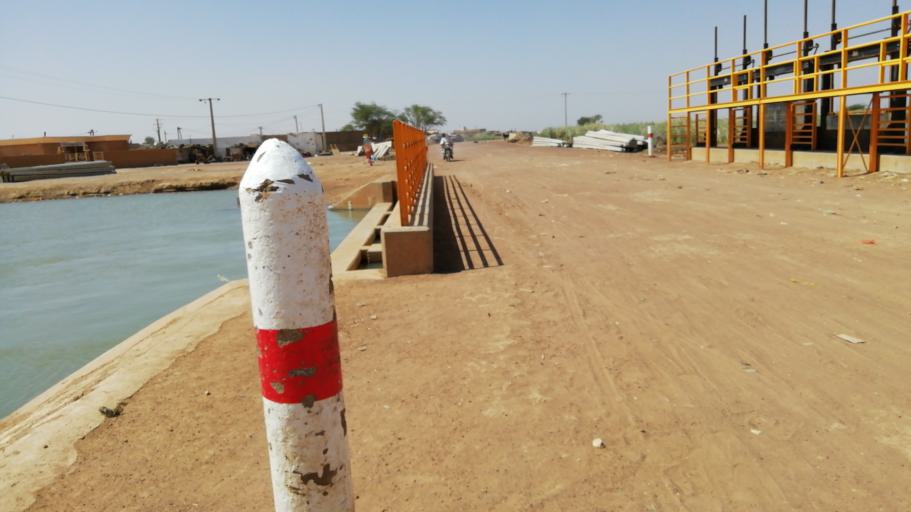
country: SN
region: Saint-Louis
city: Rosso
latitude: 16.4012
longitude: -16.0741
